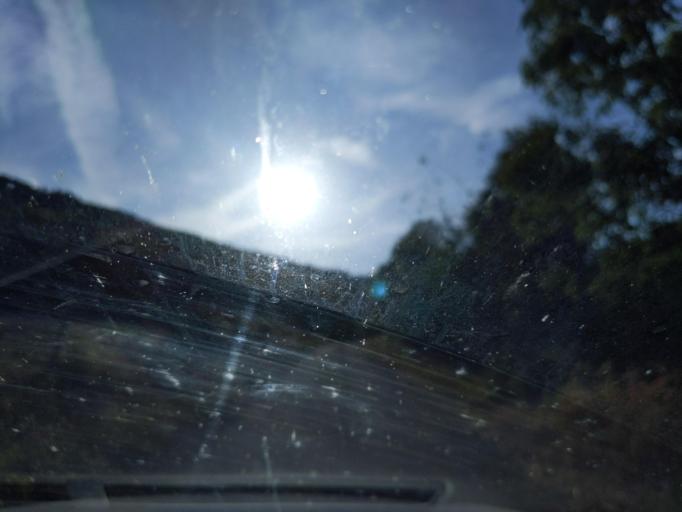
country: ES
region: La Rioja
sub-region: Provincia de La Rioja
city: Ojacastro
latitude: 42.3734
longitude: -2.9922
